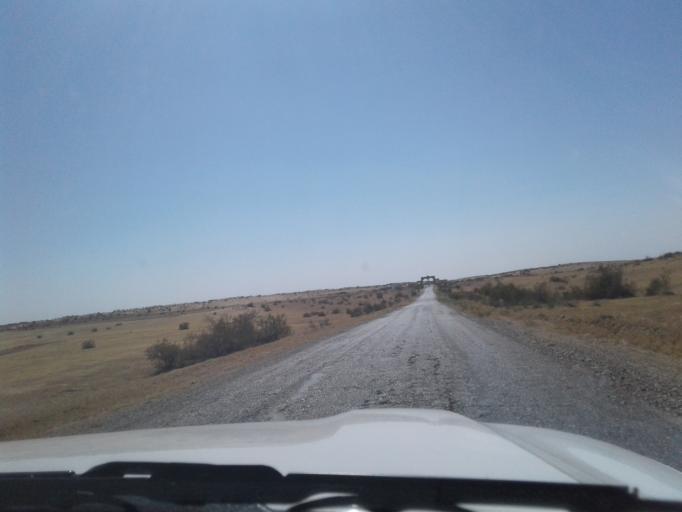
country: TM
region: Mary
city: Serhetabat
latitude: 35.9839
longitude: 62.6361
